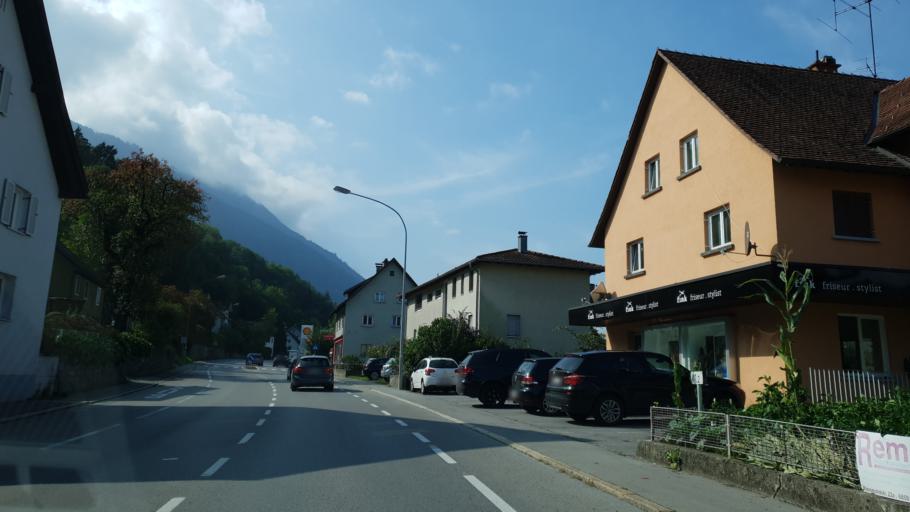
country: AT
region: Vorarlberg
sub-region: Politischer Bezirk Feldkirch
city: Feldkirch
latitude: 47.2319
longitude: 9.5871
